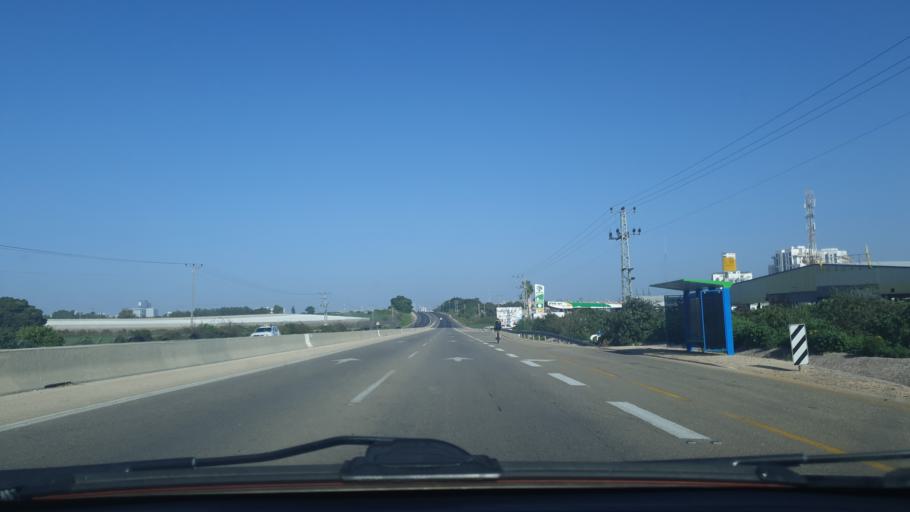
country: IL
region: Central District
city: Bet Dagan
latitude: 31.9883
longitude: 34.8304
